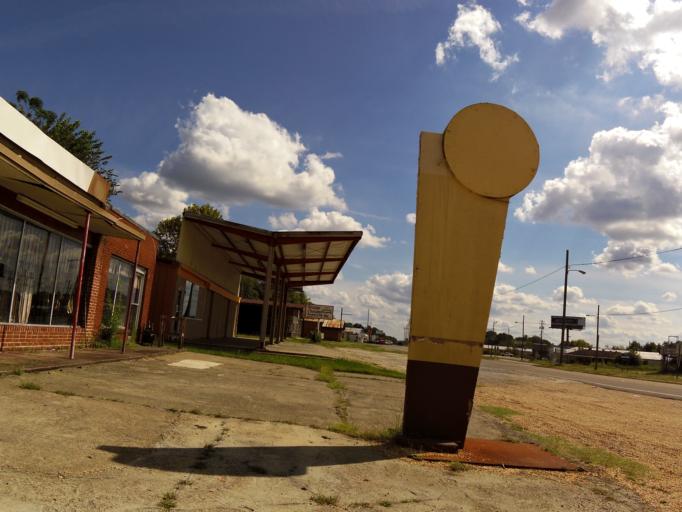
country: US
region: Alabama
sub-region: Dallas County
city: Selma
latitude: 32.4027
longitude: -87.0166
